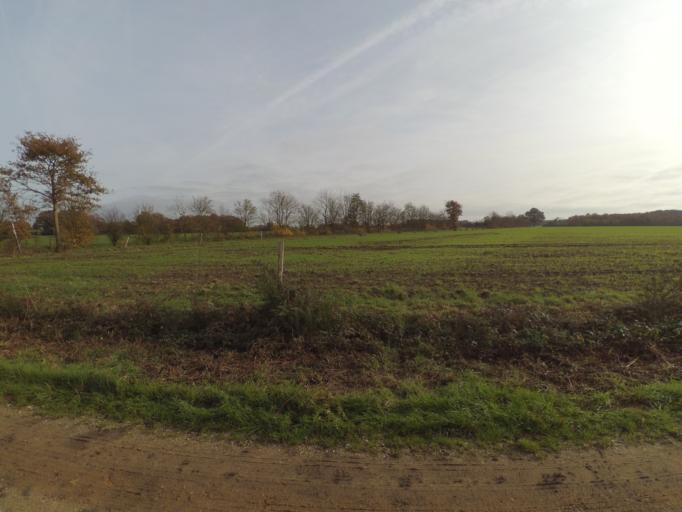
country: FR
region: Pays de la Loire
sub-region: Departement de la Loire-Atlantique
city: La Planche
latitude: 47.0070
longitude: -1.4013
